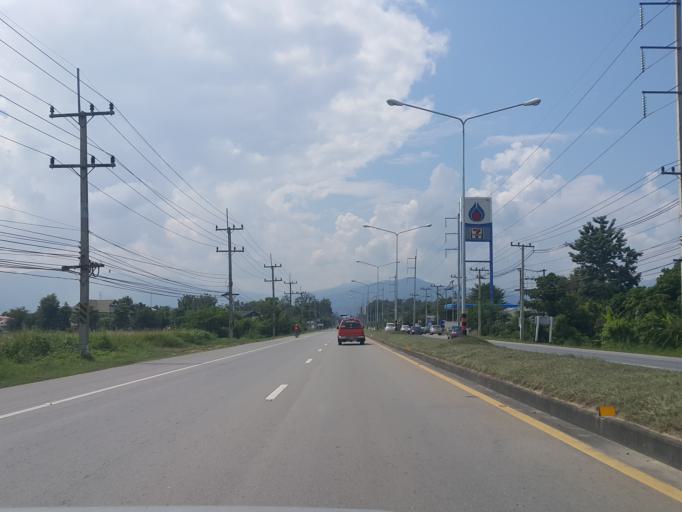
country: TH
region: Lamphun
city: Wiang Nong Long
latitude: 18.4503
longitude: 98.7114
